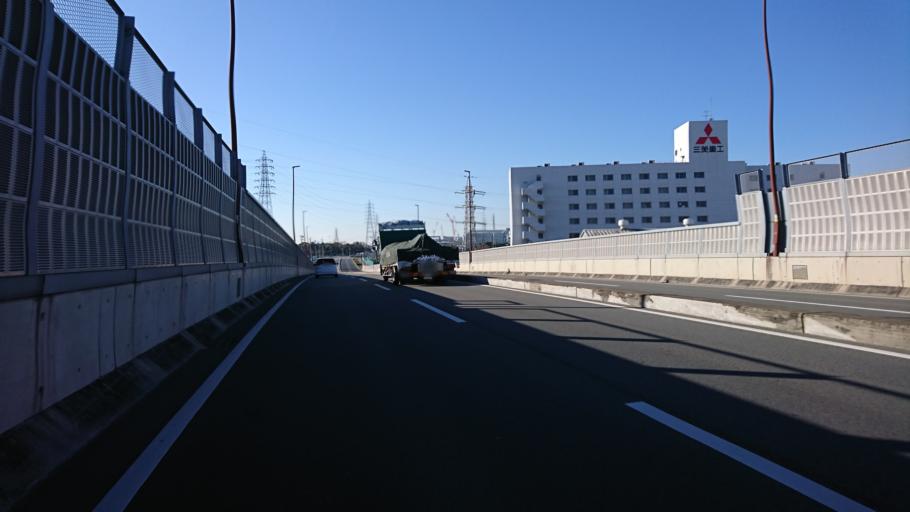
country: JP
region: Hyogo
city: Kakogawacho-honmachi
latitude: 34.7563
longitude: 134.7950
